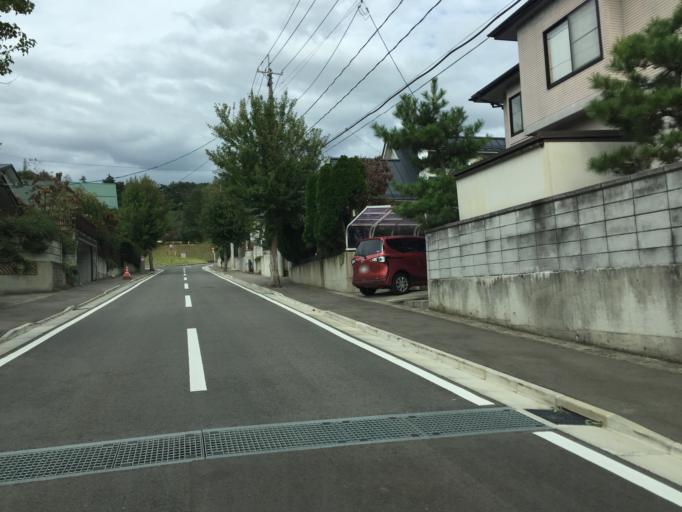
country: JP
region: Fukushima
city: Fukushima-shi
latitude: 37.6910
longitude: 140.4812
